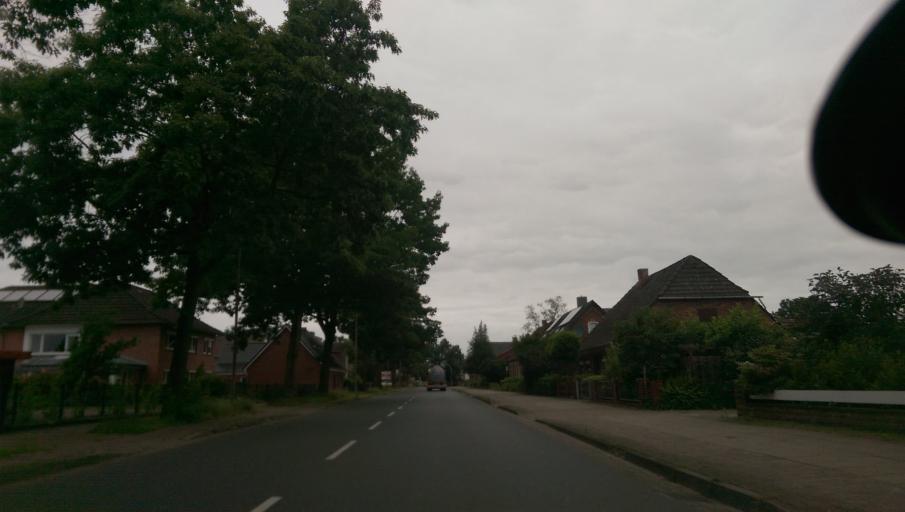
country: DE
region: Lower Saxony
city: Rotenburg
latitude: 53.1007
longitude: 9.4001
